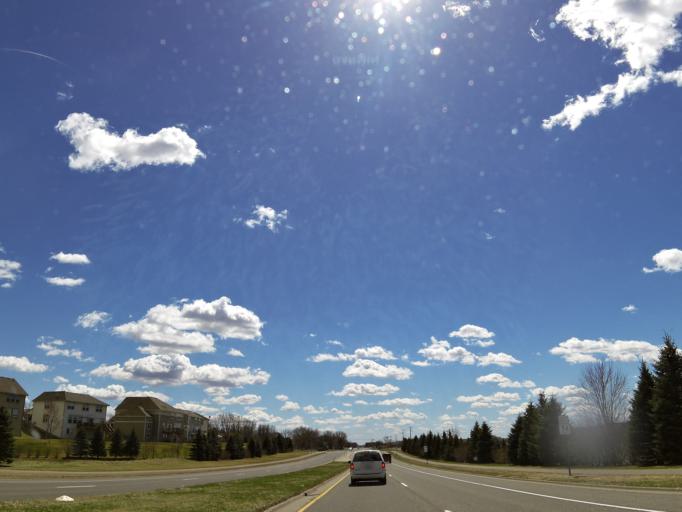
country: US
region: Minnesota
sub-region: Washington County
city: Cottage Grove
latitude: 44.8575
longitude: -92.9493
